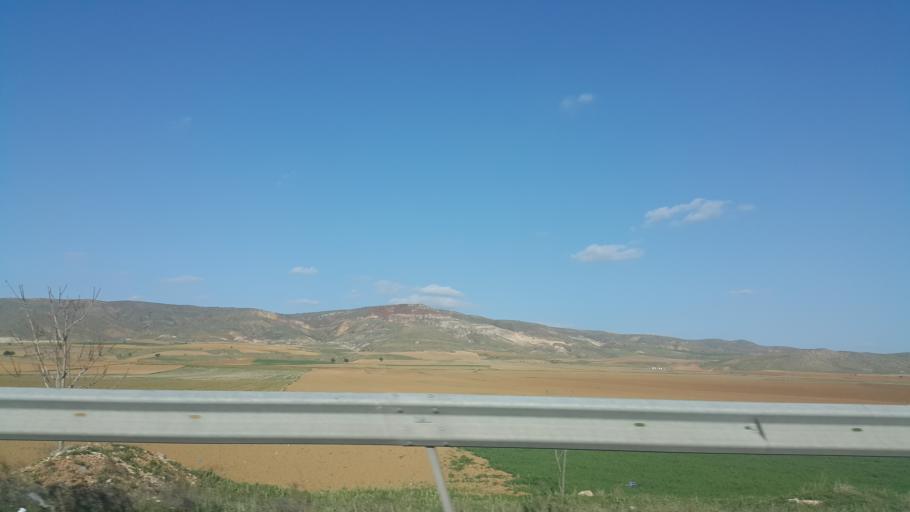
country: TR
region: Ankara
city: Sereflikochisar
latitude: 38.8915
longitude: 33.5869
